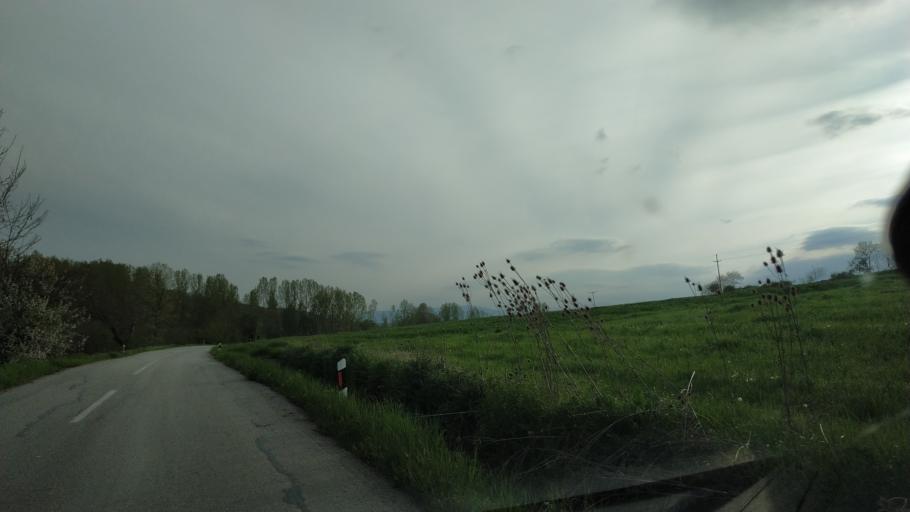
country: RS
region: Central Serbia
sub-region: Nisavski Okrug
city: Aleksinac
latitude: 43.5036
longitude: 21.8394
